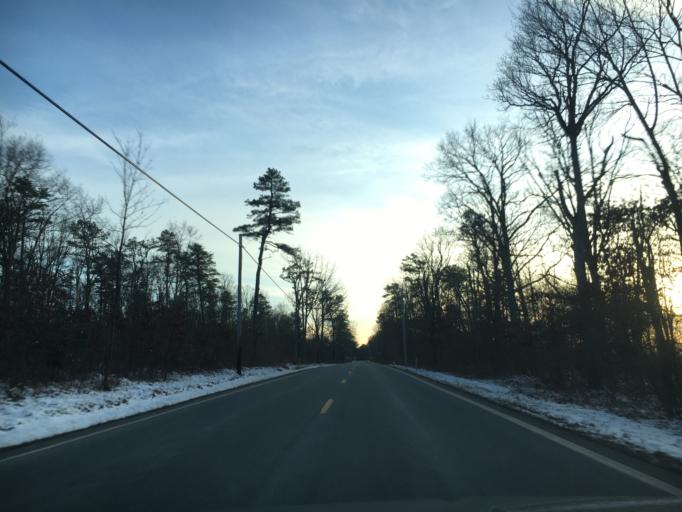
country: US
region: Pennsylvania
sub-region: Pike County
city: Hemlock Farms
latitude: 41.2372
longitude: -75.0720
